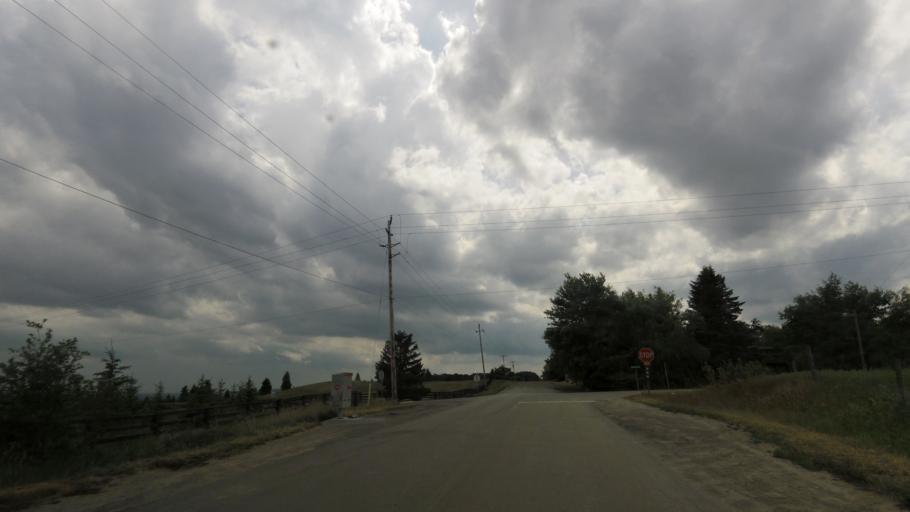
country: CA
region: Ontario
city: Orangeville
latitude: 43.8697
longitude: -79.9366
